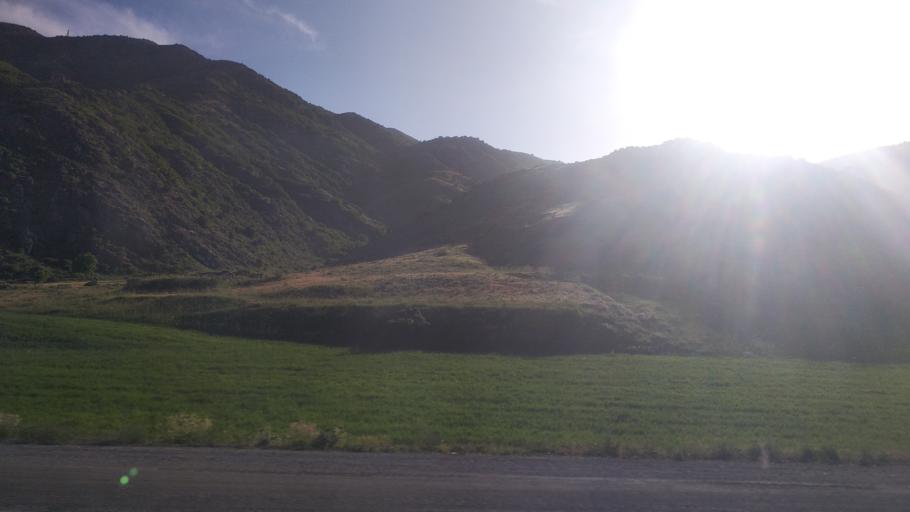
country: TR
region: Bitlis
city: Resadiye
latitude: 38.4458
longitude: 42.5435
